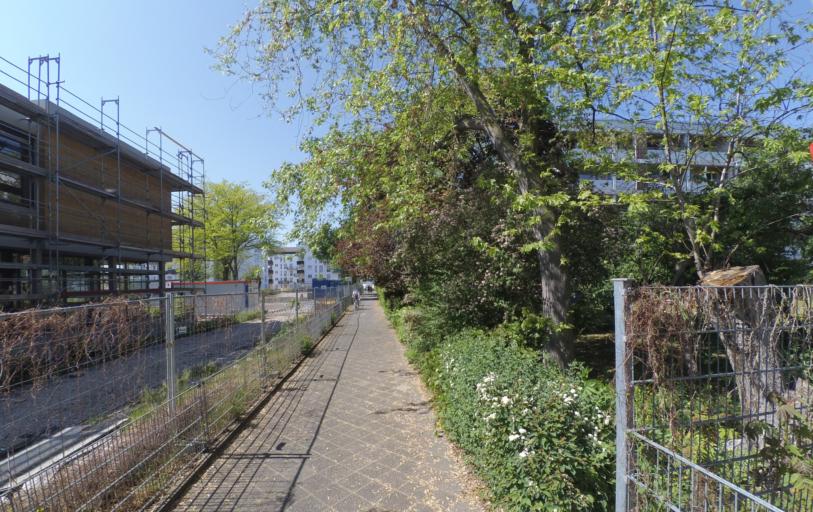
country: DE
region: Baden-Wuerttemberg
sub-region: Karlsruhe Region
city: Mannheim
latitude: 49.5229
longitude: 8.4951
